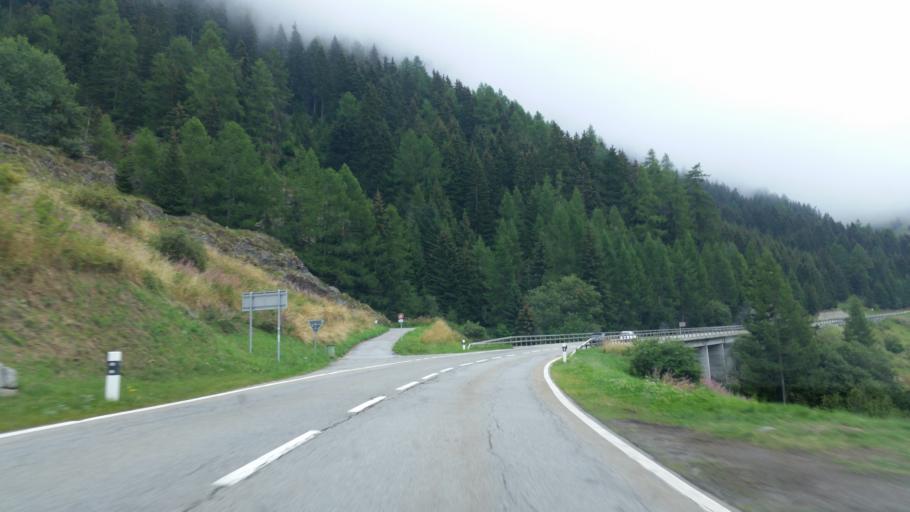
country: CH
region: Valais
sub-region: Entremont District
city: Orsieres
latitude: 45.9736
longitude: 7.2065
